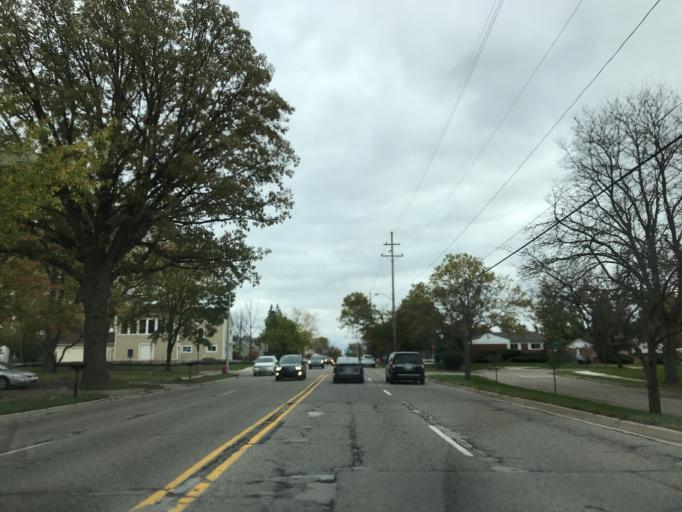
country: US
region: Michigan
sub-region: Washtenaw County
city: Ann Arbor
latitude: 42.2475
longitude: -83.7002
